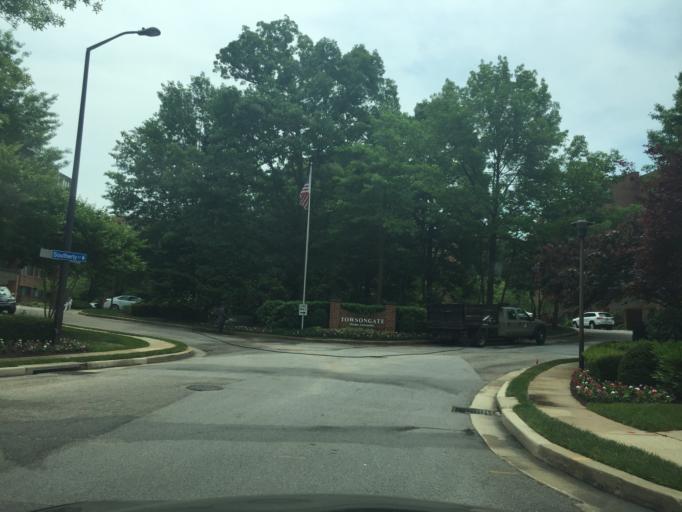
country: US
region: Maryland
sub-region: Baltimore County
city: Towson
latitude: 39.4057
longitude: -76.5967
